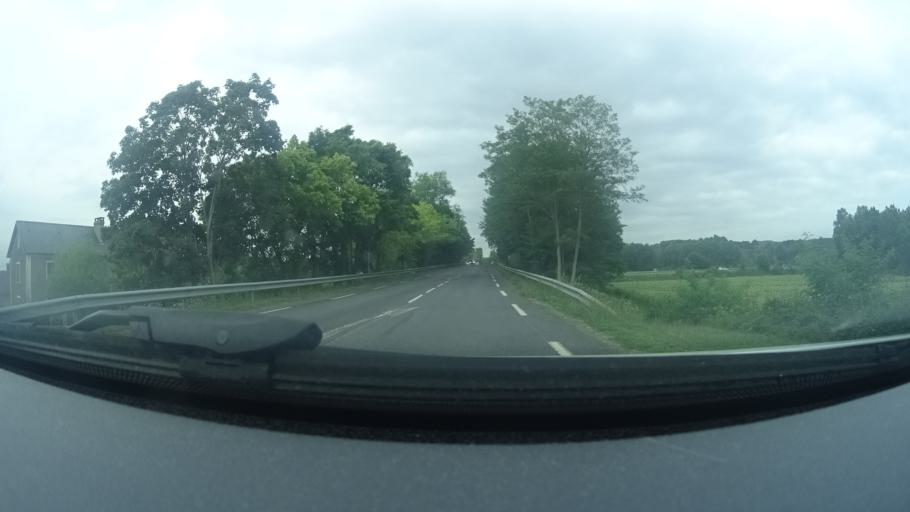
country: FR
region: Aquitaine
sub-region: Departement des Pyrenees-Atlantiques
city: Mont
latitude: 43.4475
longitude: -0.6886
